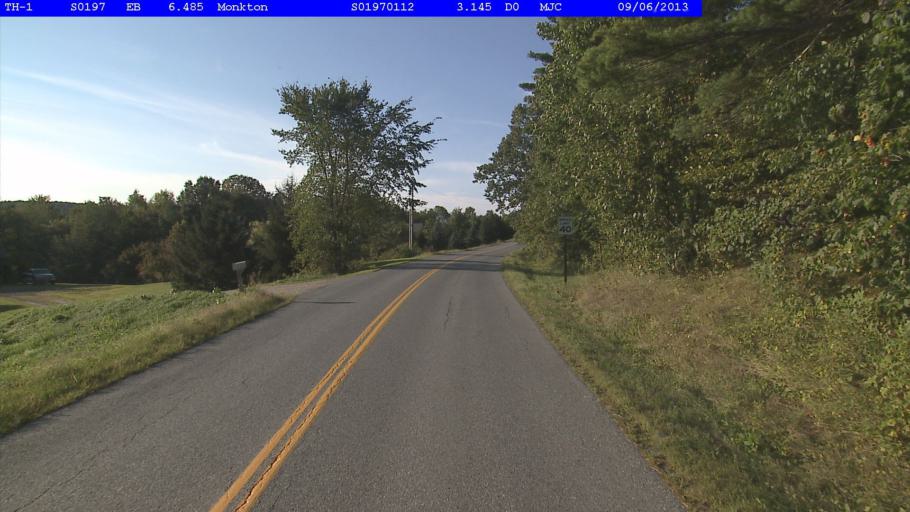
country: US
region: Vermont
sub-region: Chittenden County
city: Hinesburg
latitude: 44.2226
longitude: -73.1529
